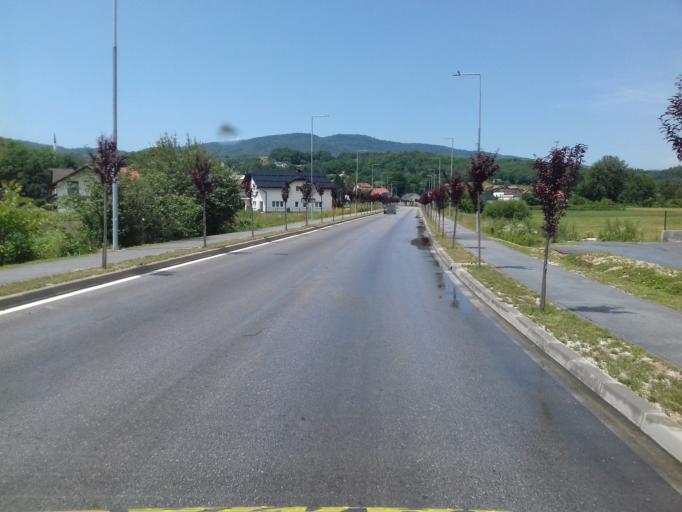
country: BA
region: Federation of Bosnia and Herzegovina
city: Kiseljak
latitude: 43.9481
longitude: 18.0788
